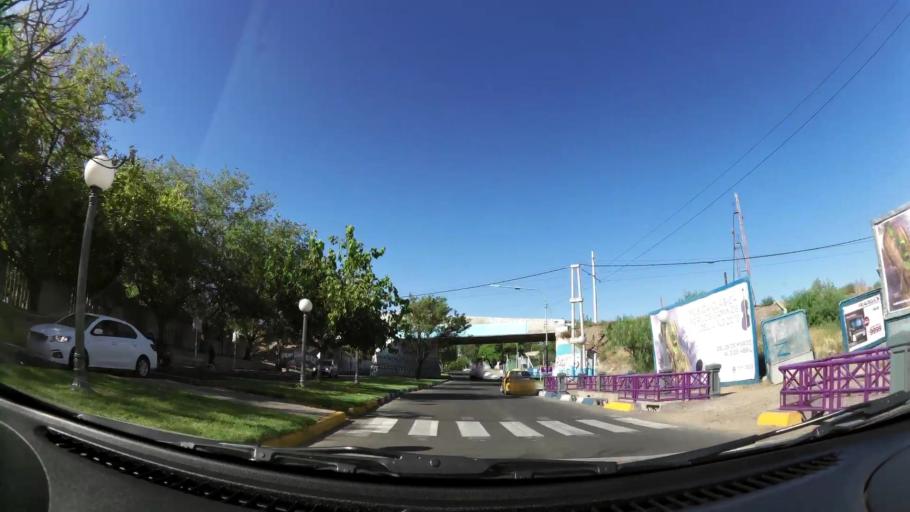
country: AR
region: Mendoza
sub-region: Departamento de Godoy Cruz
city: Godoy Cruz
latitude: -32.9199
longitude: -68.8412
